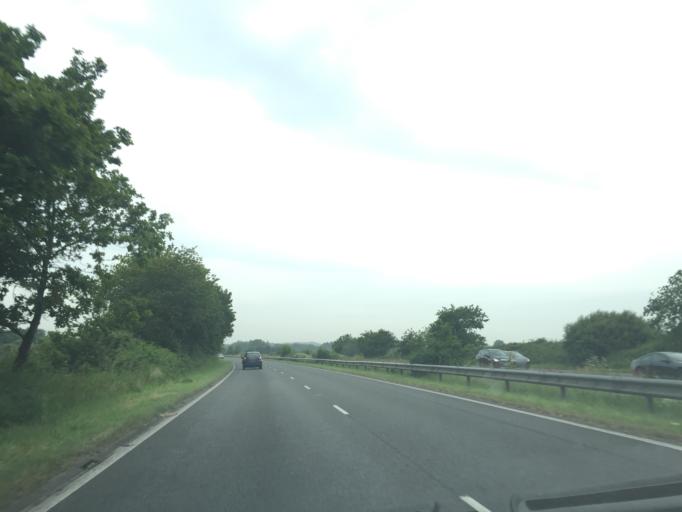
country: GB
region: England
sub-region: Dorset
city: Lytchett Matravers
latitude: 50.7390
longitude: -2.0476
